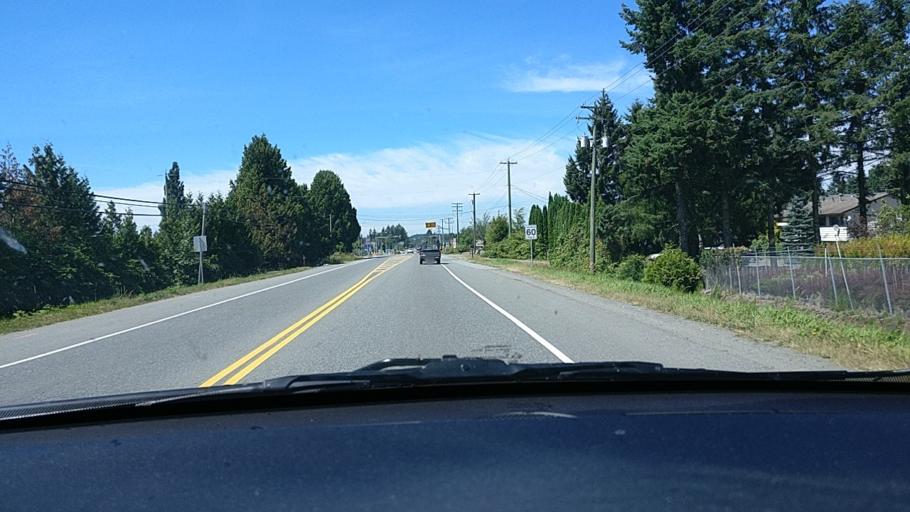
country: CA
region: British Columbia
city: Aldergrove
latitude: 49.0573
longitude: -122.4447
